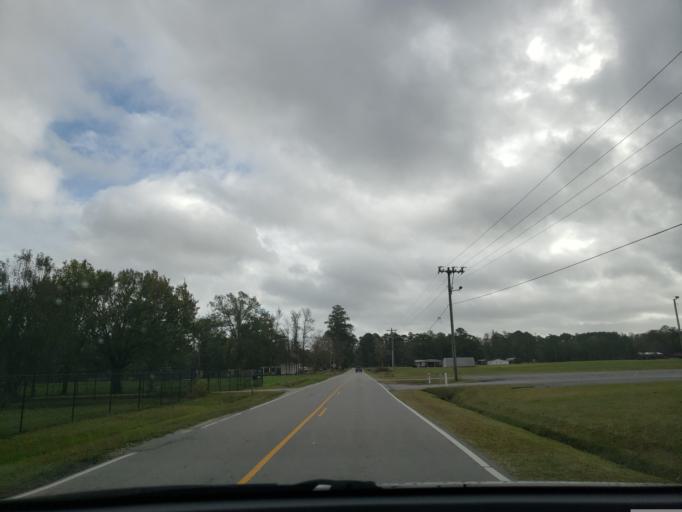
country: US
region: North Carolina
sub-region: Onslow County
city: Jacksonville
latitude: 34.7332
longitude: -77.5834
